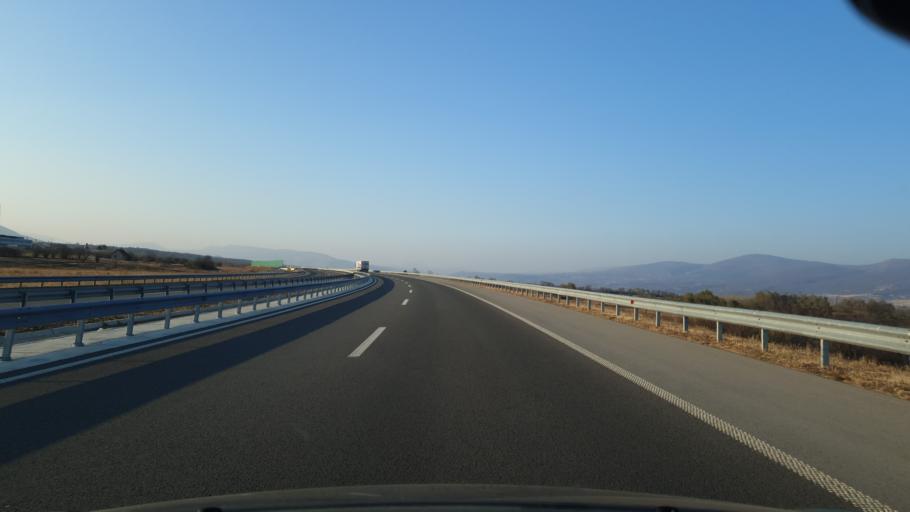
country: RS
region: Central Serbia
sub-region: Pirotski Okrug
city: Dimitrovgrad
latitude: 43.0696
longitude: 22.6774
